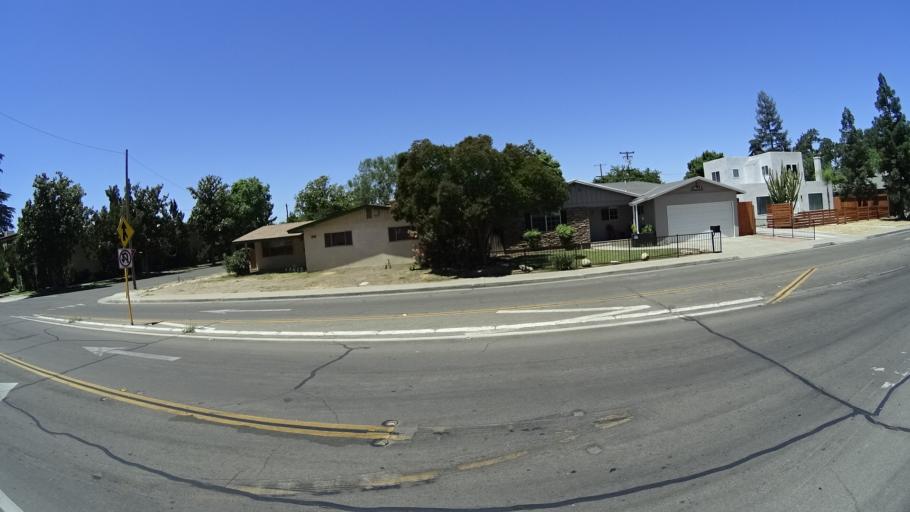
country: US
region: California
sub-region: Fresno County
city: Fresno
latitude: 36.7805
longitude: -119.8040
